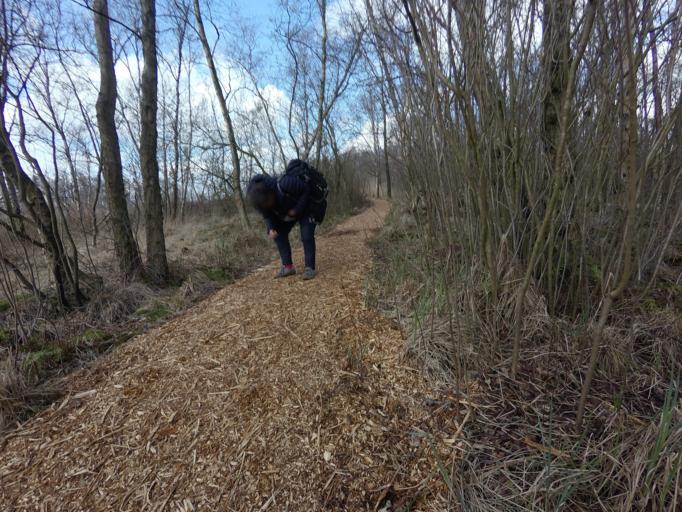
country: NL
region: Utrecht
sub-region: Gemeente De Ronde Venen
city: Mijdrecht
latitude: 52.1488
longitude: 4.8402
